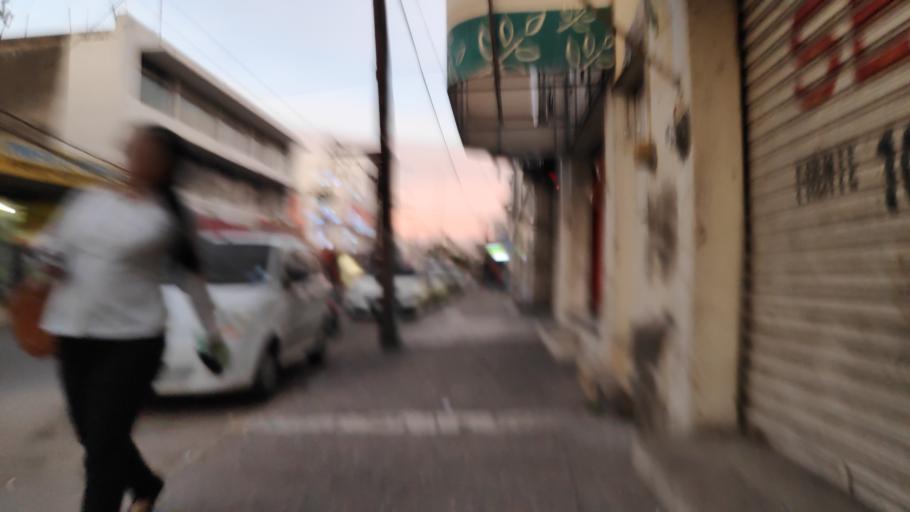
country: MX
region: Sinaloa
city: Culiacan
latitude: 24.8050
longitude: -107.3960
